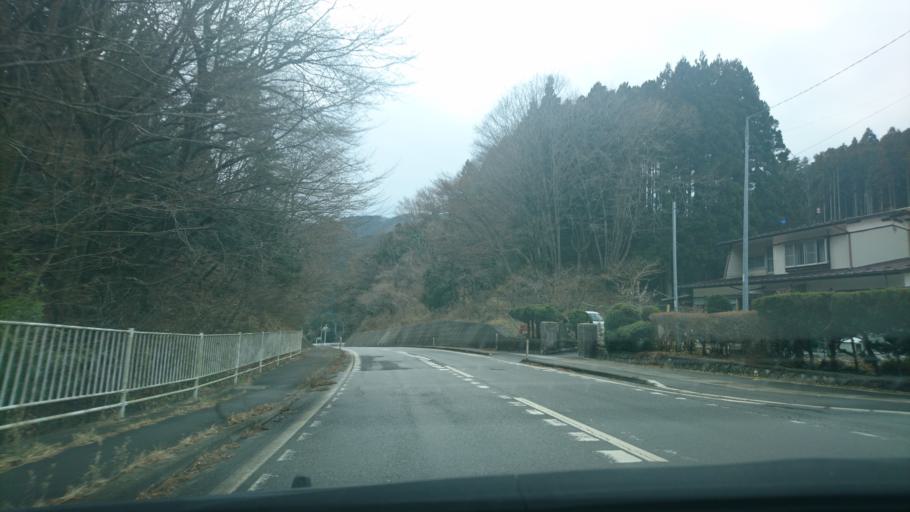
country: JP
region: Iwate
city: Ofunato
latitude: 39.1455
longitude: 141.8254
